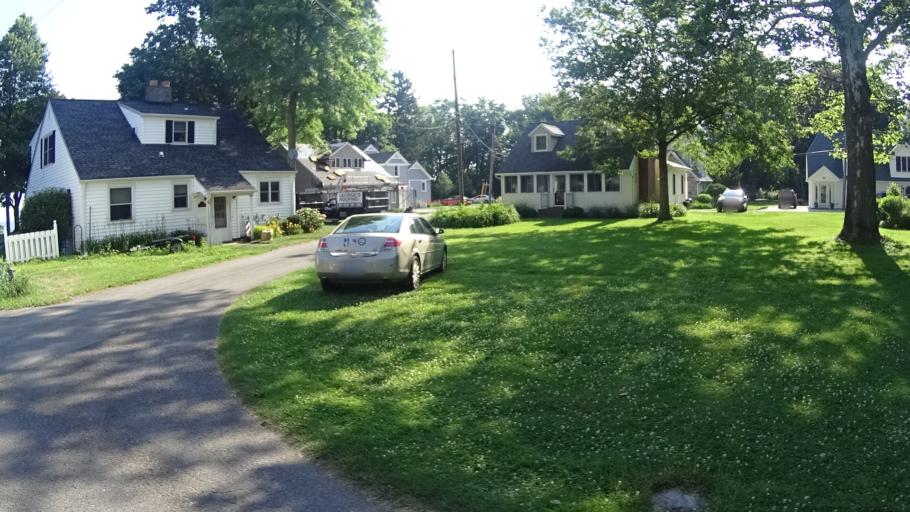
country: US
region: Ohio
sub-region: Lorain County
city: Vermilion
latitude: 41.3878
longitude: -82.4549
